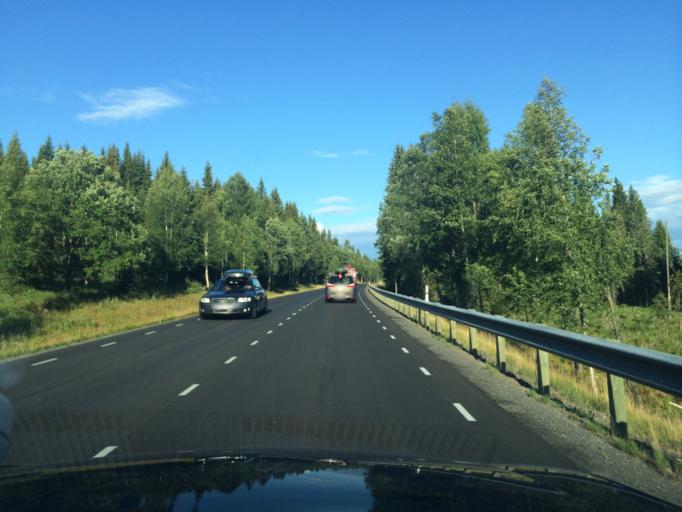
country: NO
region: Hedmark
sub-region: Elverum
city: Elverum
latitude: 61.0486
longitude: 11.9043
